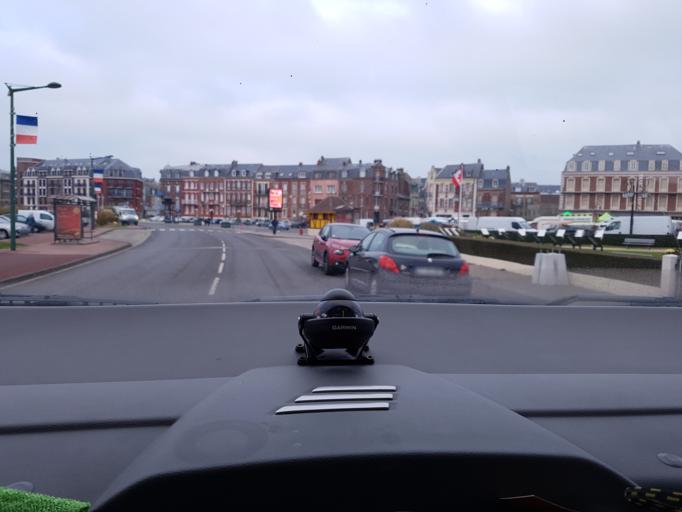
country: FR
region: Picardie
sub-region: Departement de la Somme
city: Mers-les-Bains
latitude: 50.0663
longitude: 1.3869
